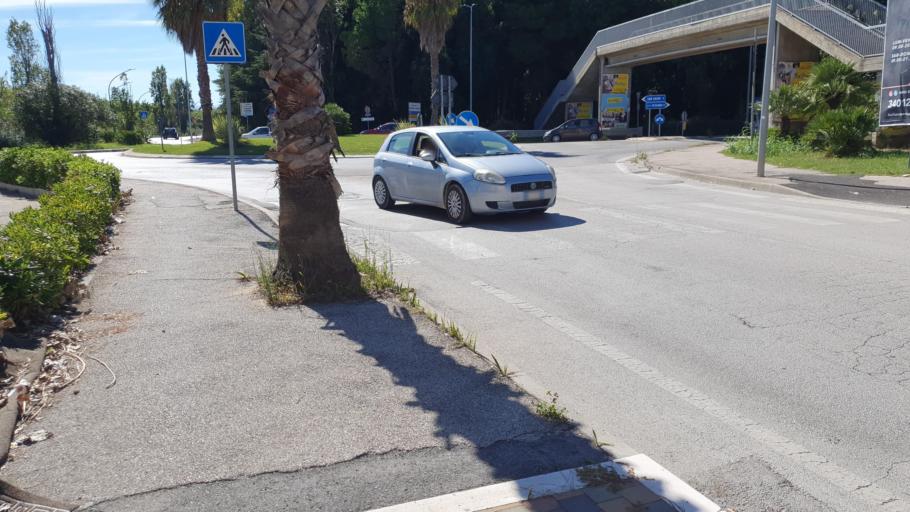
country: IT
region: Abruzzo
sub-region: Provincia di Chieti
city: Salvo Marina
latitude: 42.0670
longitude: 14.7754
